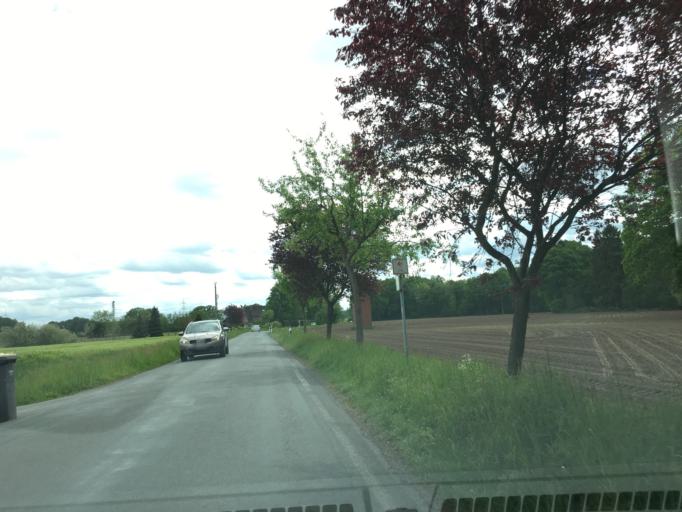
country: DE
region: North Rhine-Westphalia
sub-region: Regierungsbezirk Munster
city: Havixbeck
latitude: 51.9767
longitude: 7.4695
